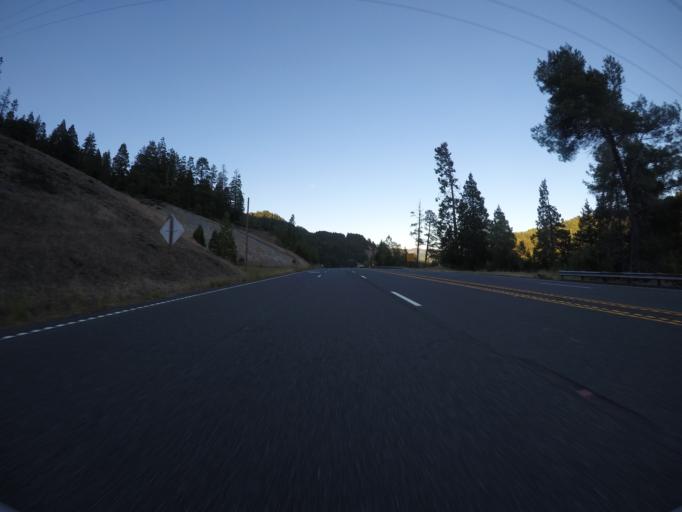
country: US
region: California
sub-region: Mendocino County
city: Laytonville
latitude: 39.8339
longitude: -123.6394
